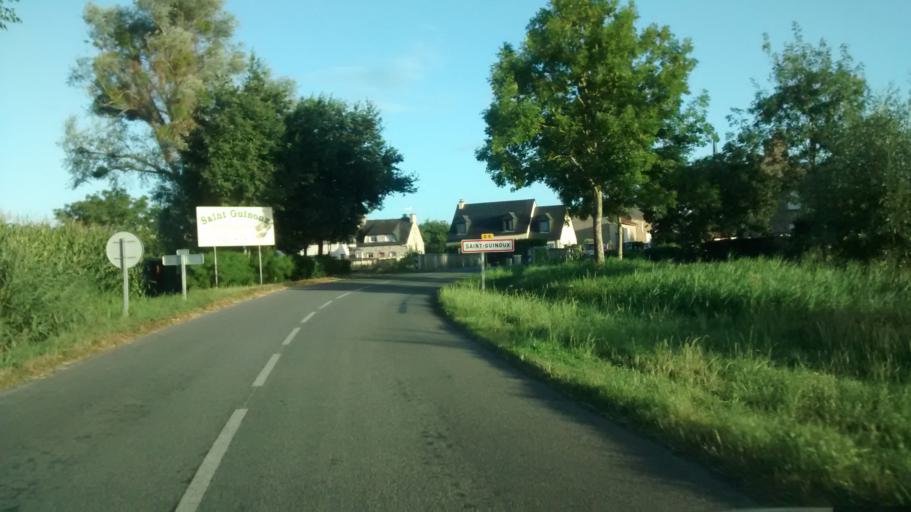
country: FR
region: Brittany
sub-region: Departement d'Ille-et-Vilaine
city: La Gouesniere
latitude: 48.5734
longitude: -1.8815
